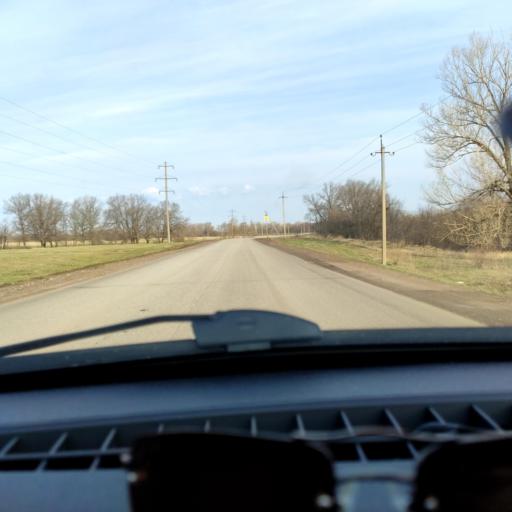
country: RU
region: Bashkortostan
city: Kabakovo
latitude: 54.5643
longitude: 55.9932
